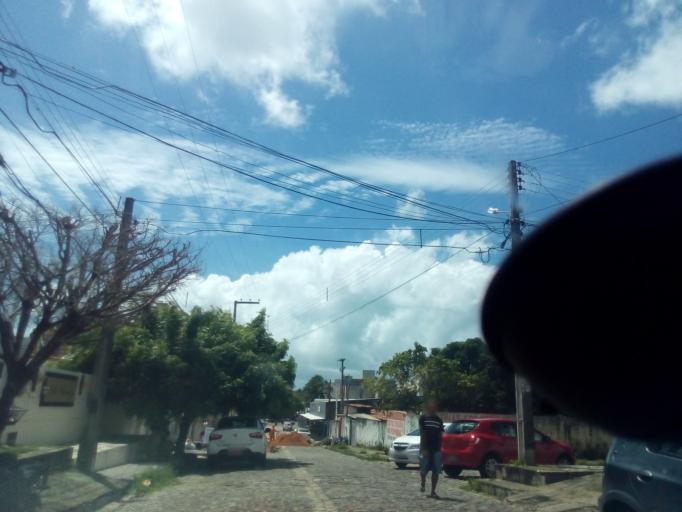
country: BR
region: Rio Grande do Norte
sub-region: Parnamirim
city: Parnamirim
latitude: -5.8869
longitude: -35.2009
